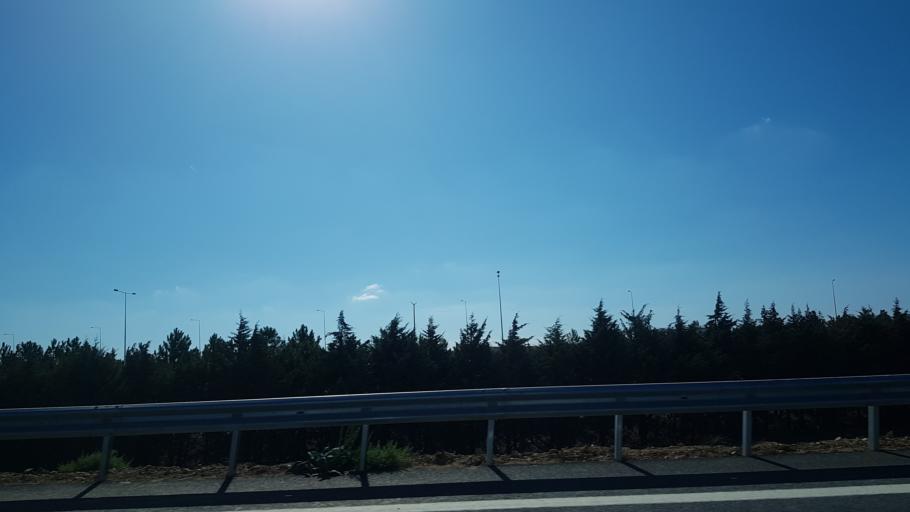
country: TR
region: Istanbul
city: Silivri
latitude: 41.1178
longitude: 28.1806
